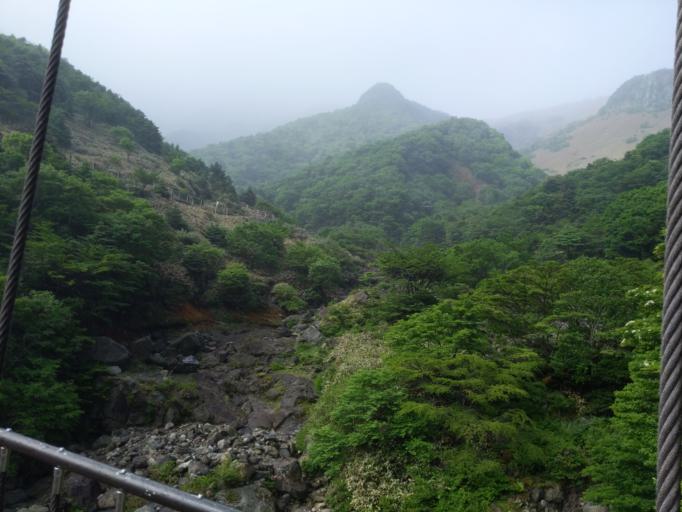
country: KR
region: Jeju-do
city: Seogwipo
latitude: 33.3726
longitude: 126.5296
